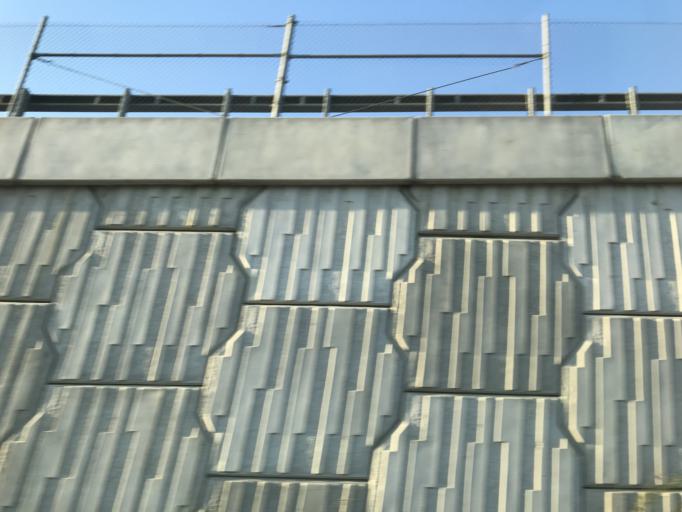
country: TR
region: Bursa
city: Gemlik
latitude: 40.4198
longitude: 29.1665
